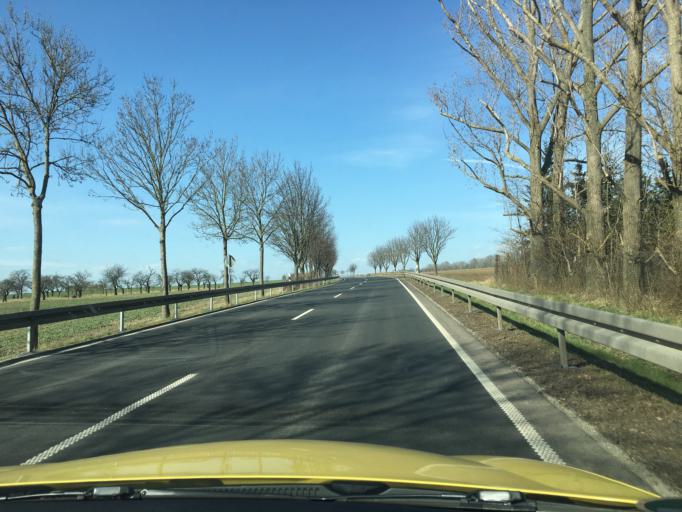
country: DE
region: Thuringia
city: Buttelstedt
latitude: 51.0816
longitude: 11.3477
